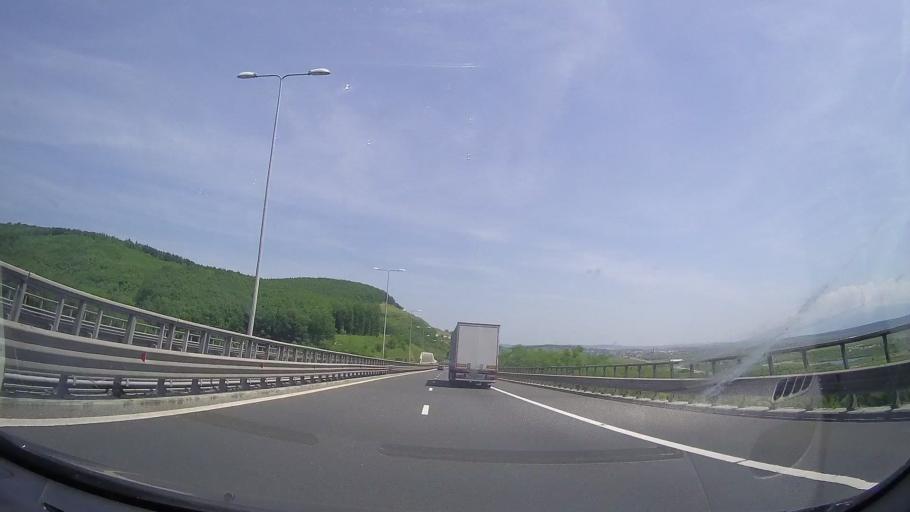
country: RO
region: Sibiu
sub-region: Comuna Orlat
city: Orlat
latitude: 45.7830
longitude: 23.9727
